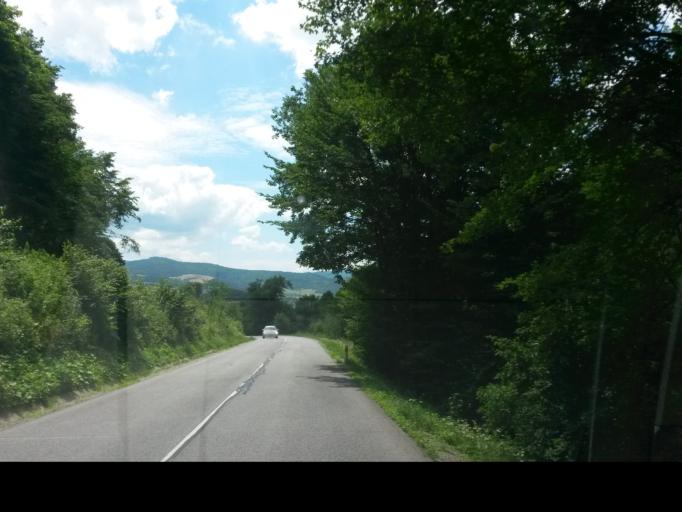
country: SK
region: Kosicky
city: Gelnica
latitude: 48.8997
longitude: 21.0212
